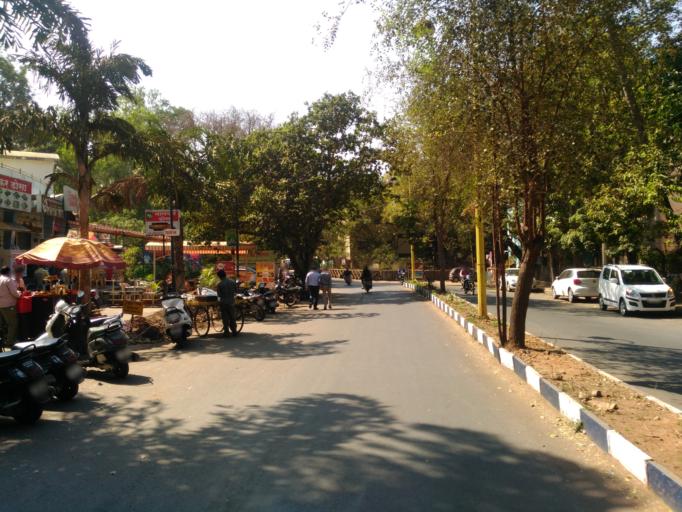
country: IN
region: Maharashtra
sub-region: Pune Division
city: Pune
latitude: 18.4810
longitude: 73.8539
